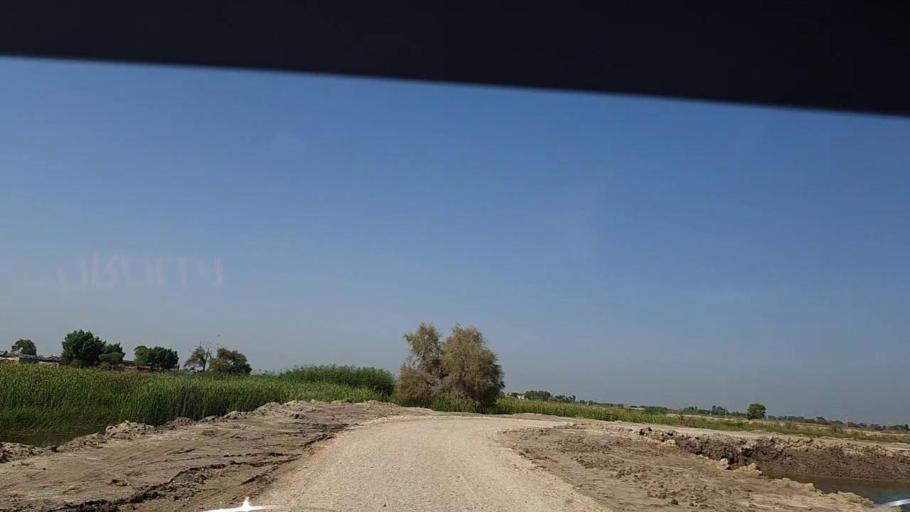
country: PK
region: Sindh
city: Tangwani
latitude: 28.3221
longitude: 69.0832
